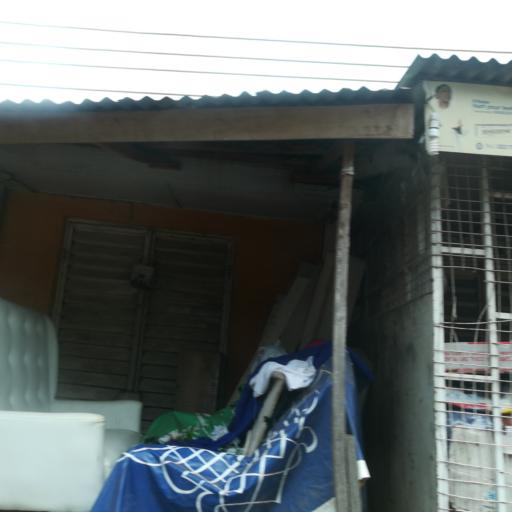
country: NG
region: Lagos
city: Agege
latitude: 6.6024
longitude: 3.2983
